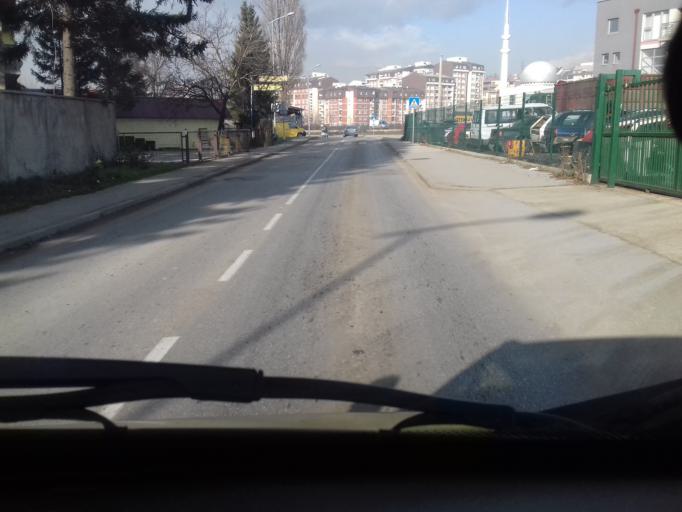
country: BA
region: Federation of Bosnia and Herzegovina
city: Zenica
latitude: 44.1926
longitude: 17.9334
